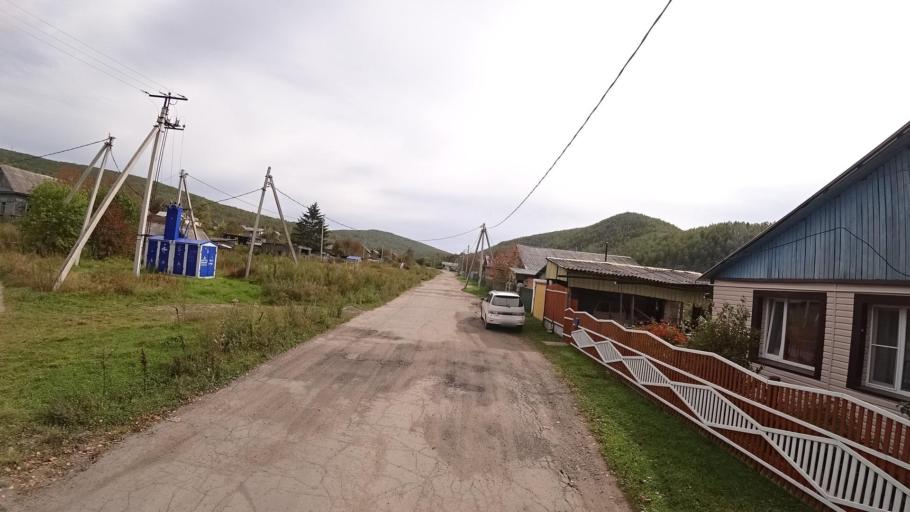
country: RU
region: Jewish Autonomous Oblast
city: Khingansk
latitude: 49.1238
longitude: 131.2039
